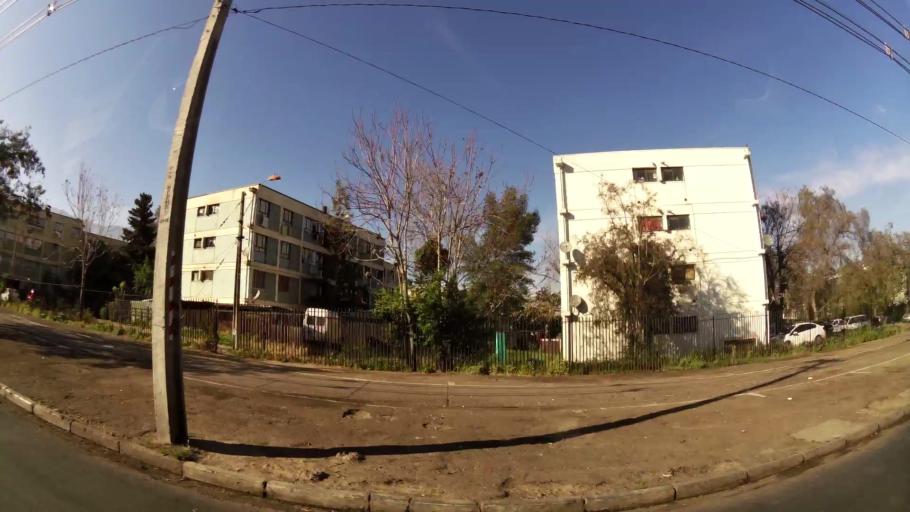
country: CL
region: Santiago Metropolitan
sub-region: Provincia de Santiago
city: Villa Presidente Frei, Nunoa, Santiago, Chile
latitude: -33.4626
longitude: -70.5558
